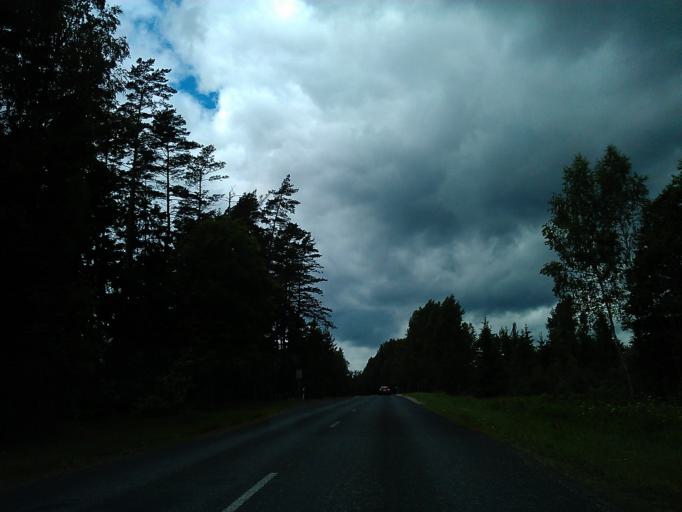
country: LV
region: Talsu Rajons
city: Stende
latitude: 57.0910
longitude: 22.3925
